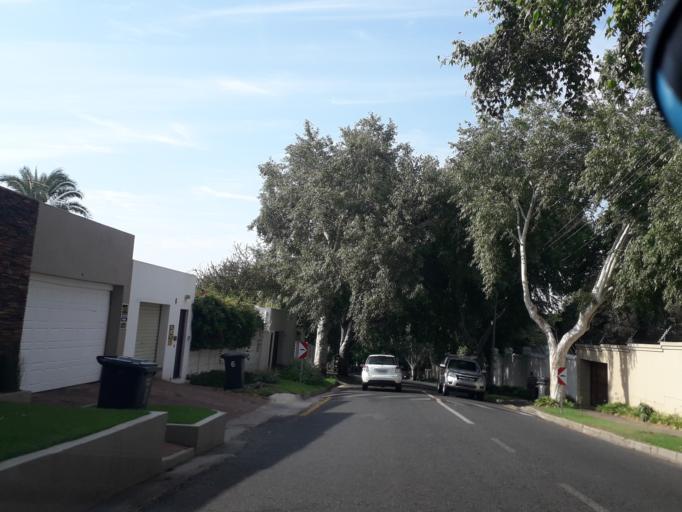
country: ZA
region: Gauteng
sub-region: City of Johannesburg Metropolitan Municipality
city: Johannesburg
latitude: -26.1470
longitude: 28.0250
